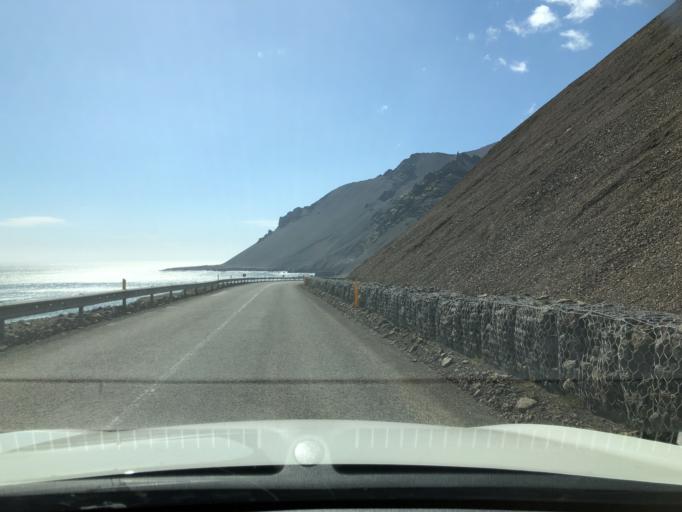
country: IS
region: East
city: Reydarfjoerdur
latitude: 64.4692
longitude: -14.5010
